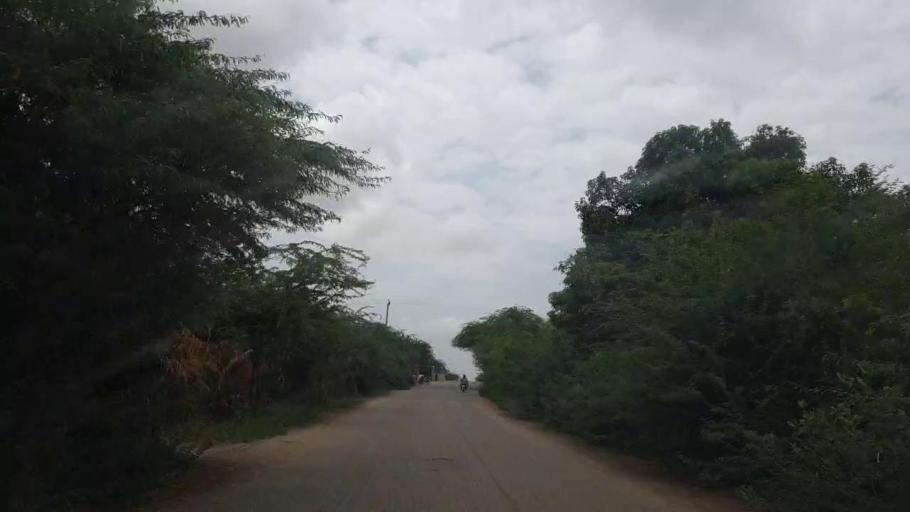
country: PK
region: Sindh
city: Naukot
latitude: 24.9024
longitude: 69.2613
